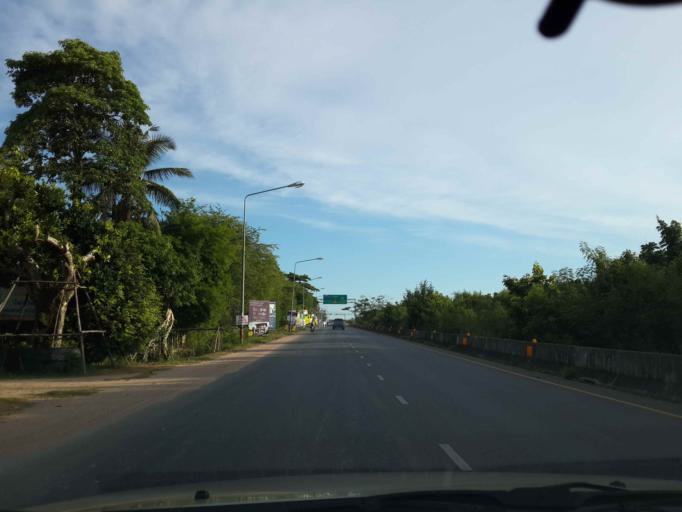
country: TH
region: Chon Buri
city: Phatthaya
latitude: 12.9516
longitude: 100.9153
